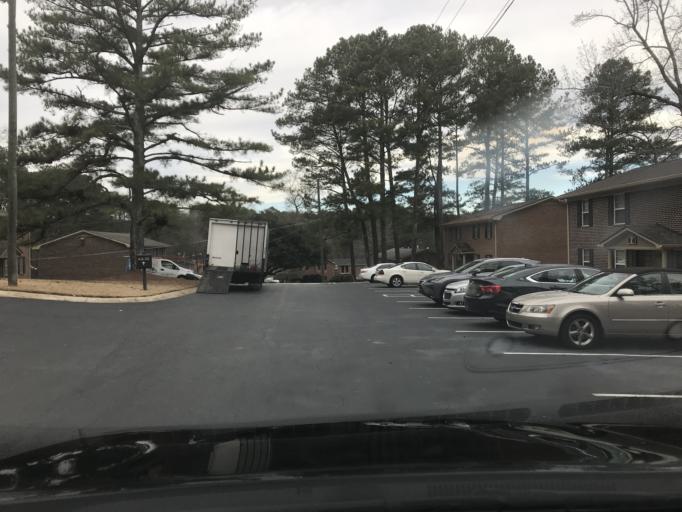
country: US
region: Georgia
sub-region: Fulton County
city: East Point
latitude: 33.7201
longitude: -84.5086
